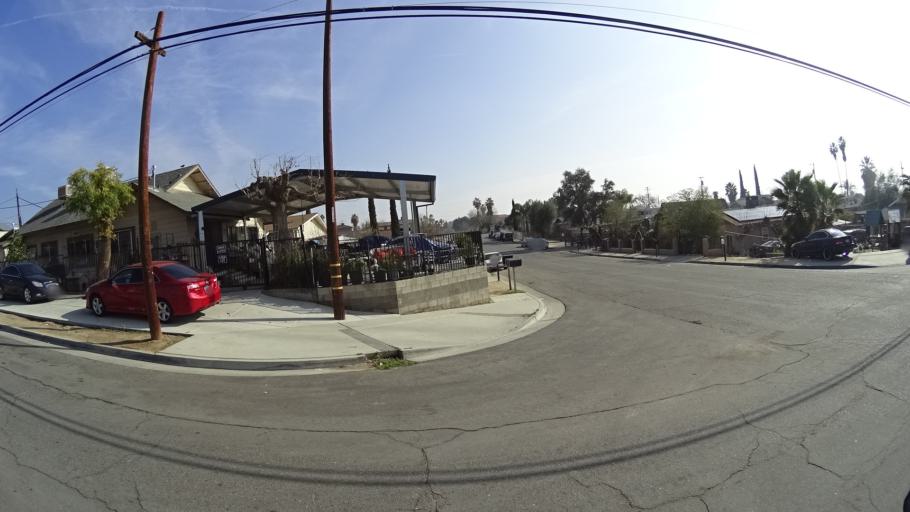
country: US
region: California
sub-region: Kern County
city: Bakersfield
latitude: 35.3844
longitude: -118.9768
